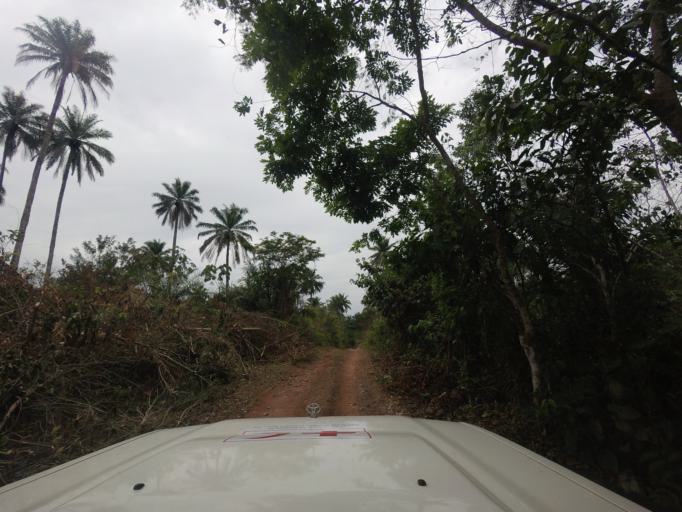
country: GN
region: Nzerekore
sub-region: Prefecture de Guekedou
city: Gueckedou
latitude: 8.4268
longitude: -10.2500
